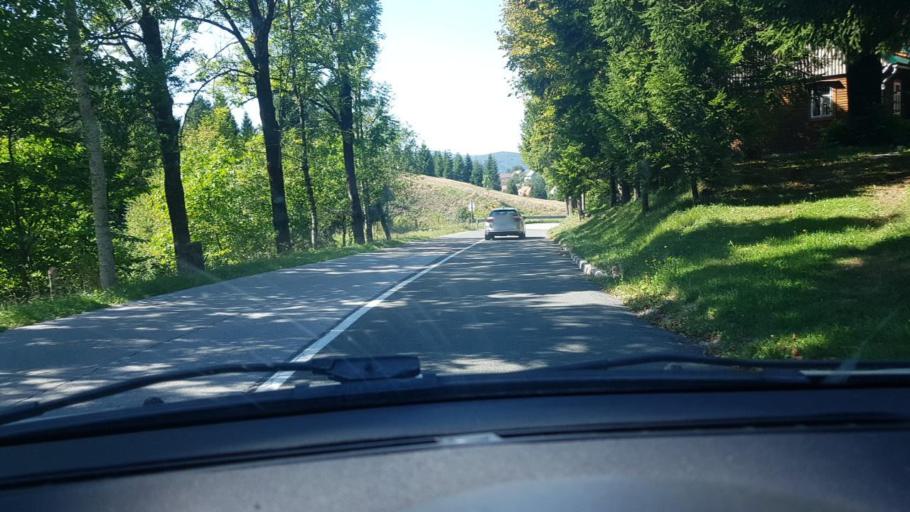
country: HR
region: Primorsko-Goranska
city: Vrbovsko
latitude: 45.3750
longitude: 14.9609
